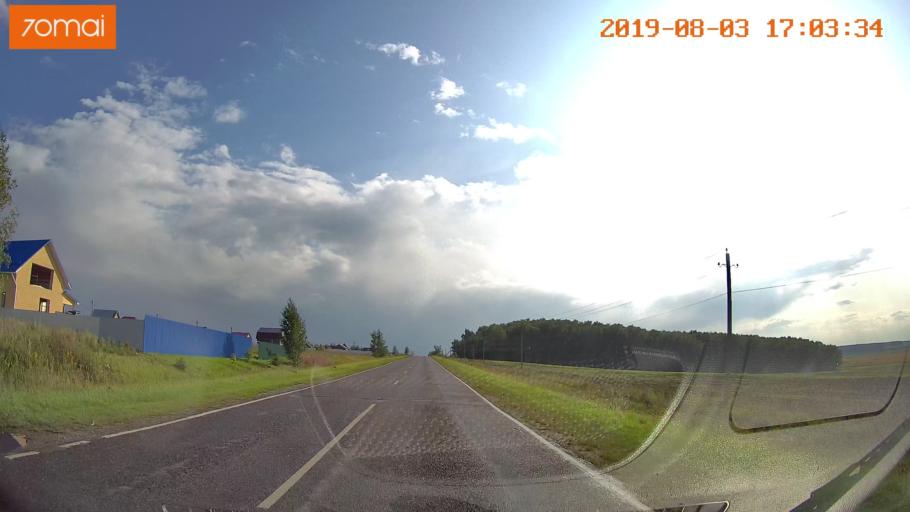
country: RU
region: Moskovskaya
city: Troitskoye
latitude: 55.3363
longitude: 38.5697
